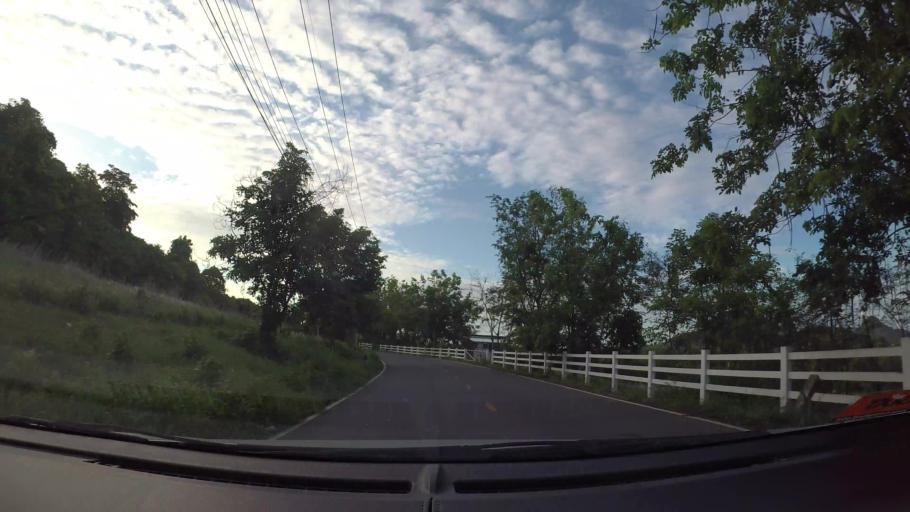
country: TH
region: Chon Buri
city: Sattahip
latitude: 12.7458
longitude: 100.9338
